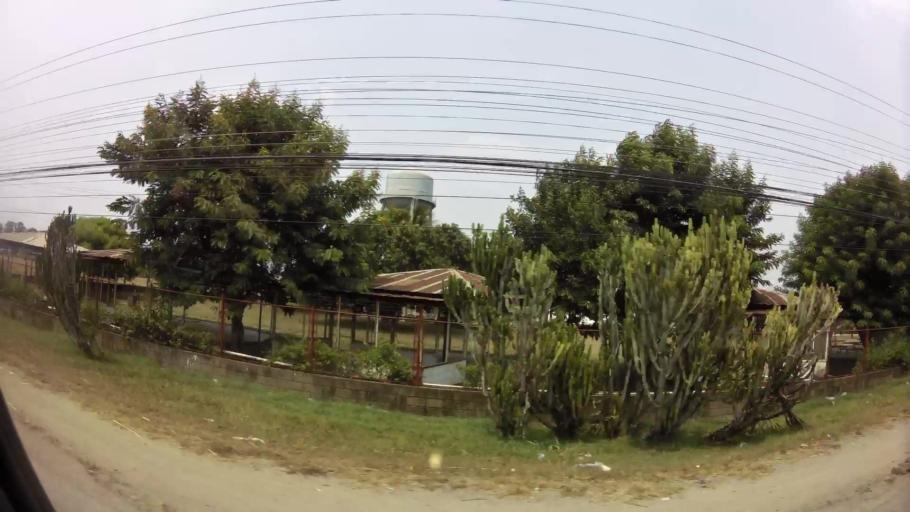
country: HN
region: Cortes
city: La Lima
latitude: 15.4339
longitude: -87.9033
